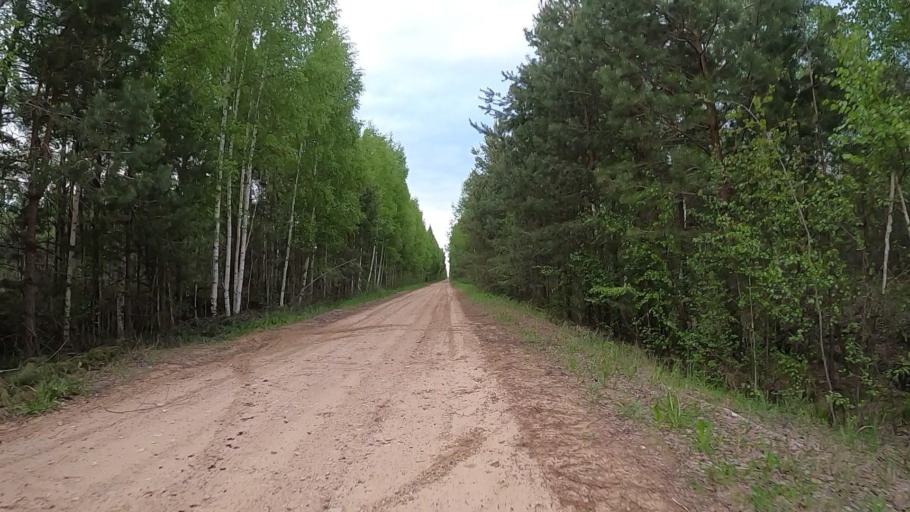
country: LV
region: Olaine
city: Olaine
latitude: 56.8450
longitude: 23.9360
